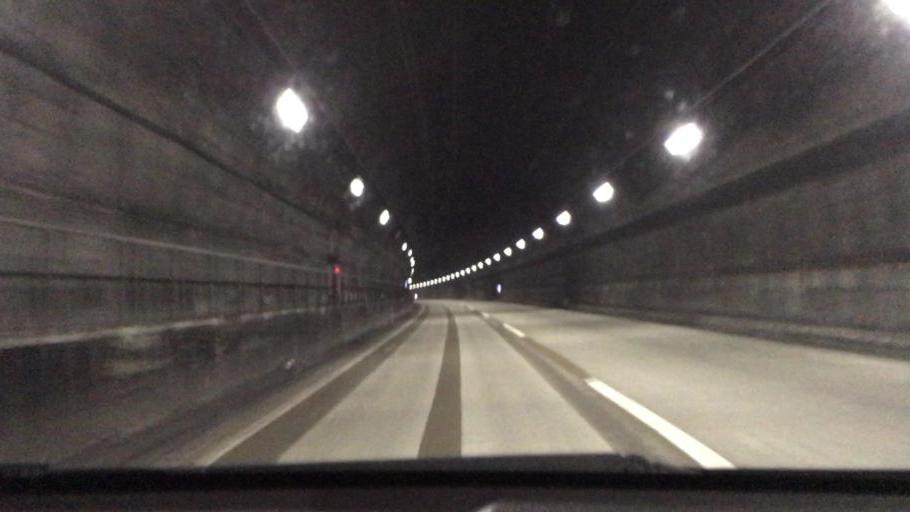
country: JP
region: Yamaguchi
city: Hofu
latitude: 34.0705
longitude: 131.6651
